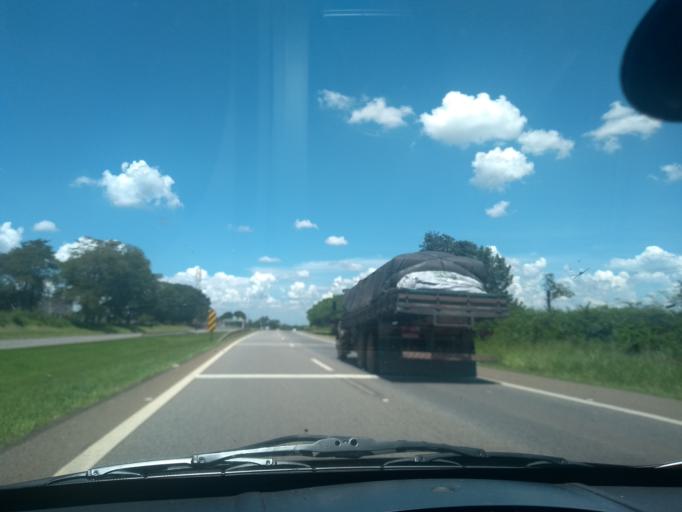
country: BR
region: Sao Paulo
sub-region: Mogi-Mirim
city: Mogi Mirim
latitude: -22.4881
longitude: -46.9813
